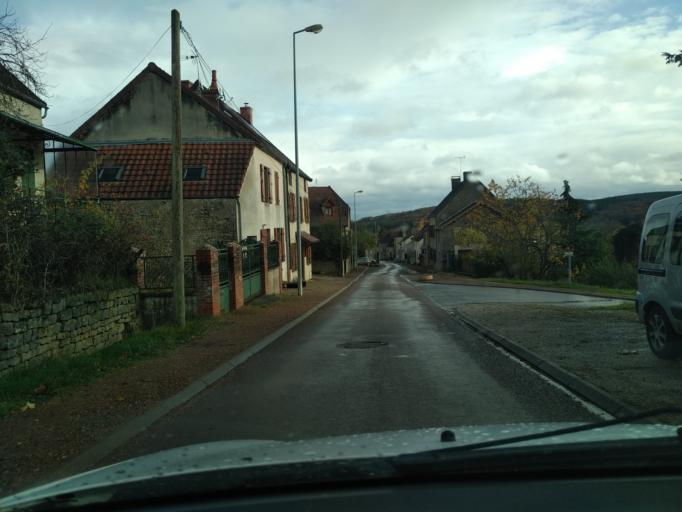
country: FR
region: Bourgogne
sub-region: Departement de Saone-et-Loire
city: Saint-Leger-sur-Dheune
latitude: 46.8393
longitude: 4.6659
